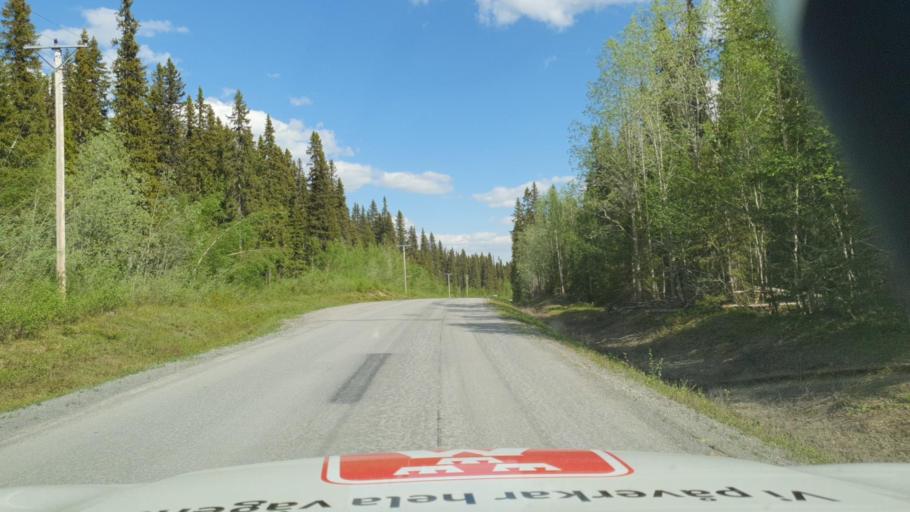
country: SE
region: Jaemtland
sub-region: Krokoms Kommun
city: Krokom
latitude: 63.6795
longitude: 14.2741
